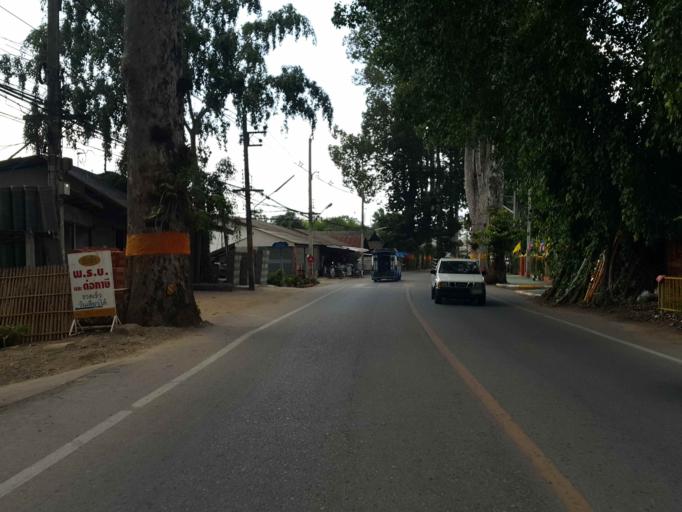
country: TH
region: Chiang Mai
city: Saraphi
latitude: 18.7052
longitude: 99.0399
